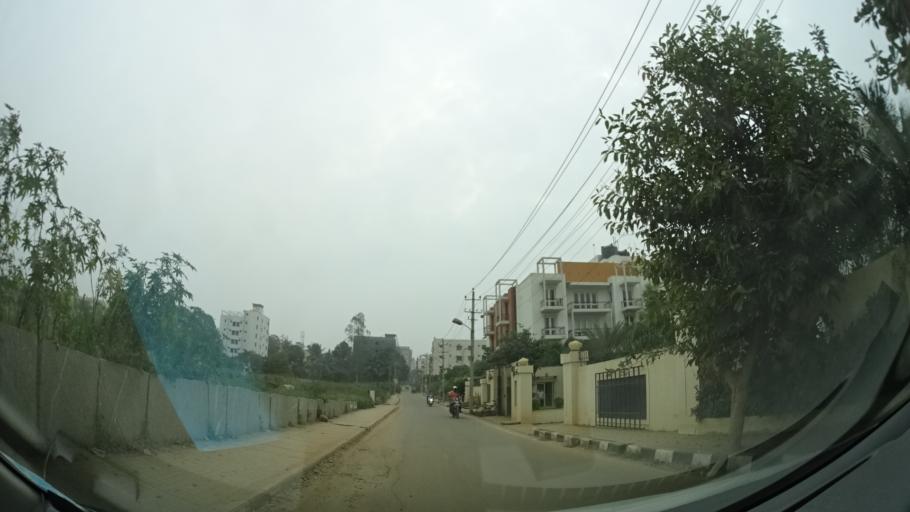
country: IN
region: Karnataka
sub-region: Bangalore Rural
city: Hoskote
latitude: 12.9800
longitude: 77.7487
